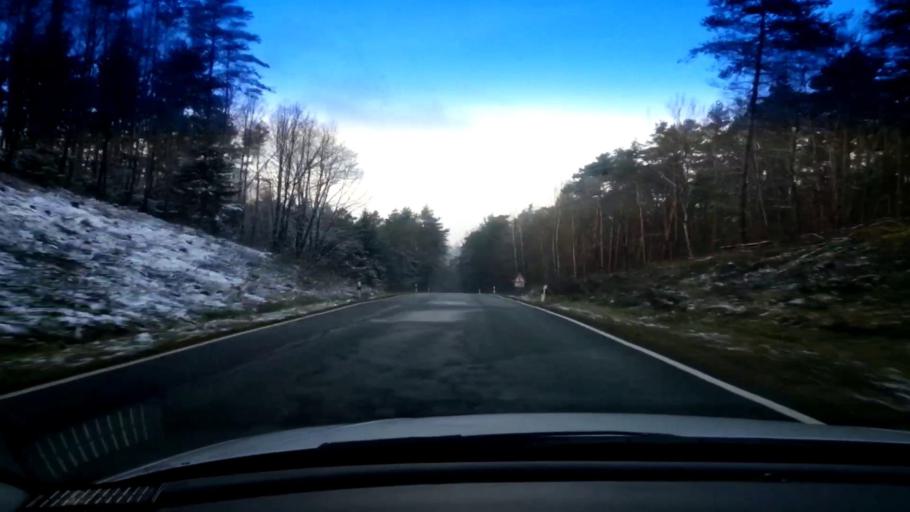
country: DE
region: Bavaria
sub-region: Upper Franconia
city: Frensdorf
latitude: 49.7770
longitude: 10.8920
